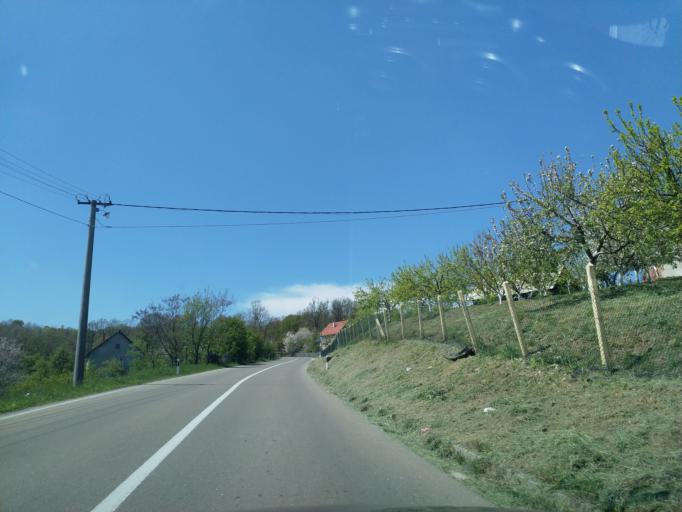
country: RS
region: Central Serbia
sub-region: Belgrade
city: Lazarevac
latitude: 44.3668
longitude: 20.3448
